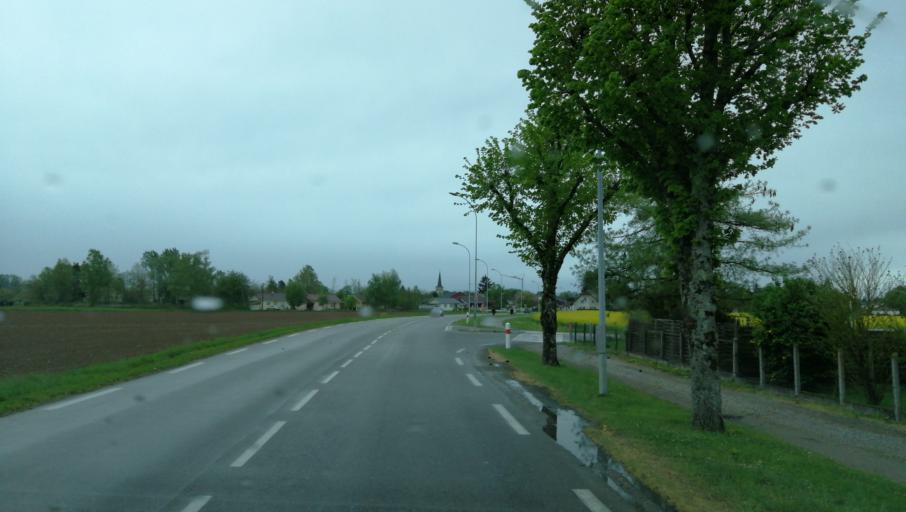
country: FR
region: Franche-Comte
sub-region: Departement du Jura
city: Bletterans
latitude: 46.7436
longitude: 5.4592
